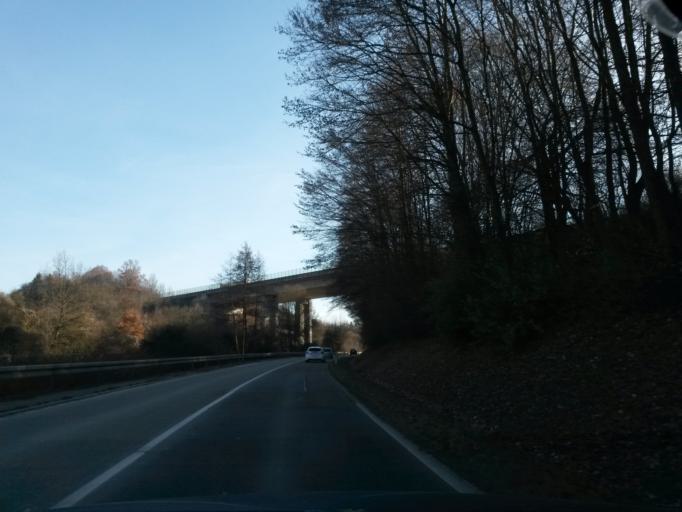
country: DE
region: Baden-Wuerttemberg
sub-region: Karlsruhe Region
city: Ispringen
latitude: 48.9099
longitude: 8.6821
